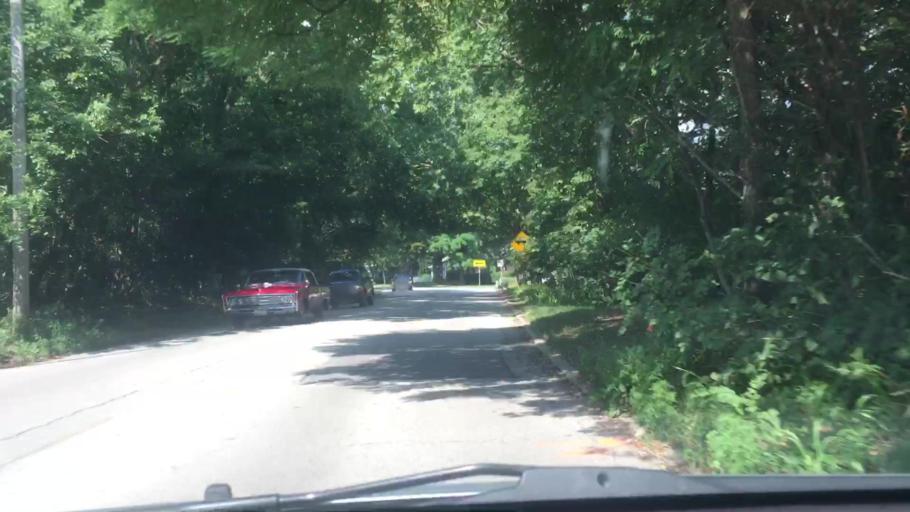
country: US
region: Illinois
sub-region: Kane County
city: Geneva
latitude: 41.8818
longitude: -88.3069
